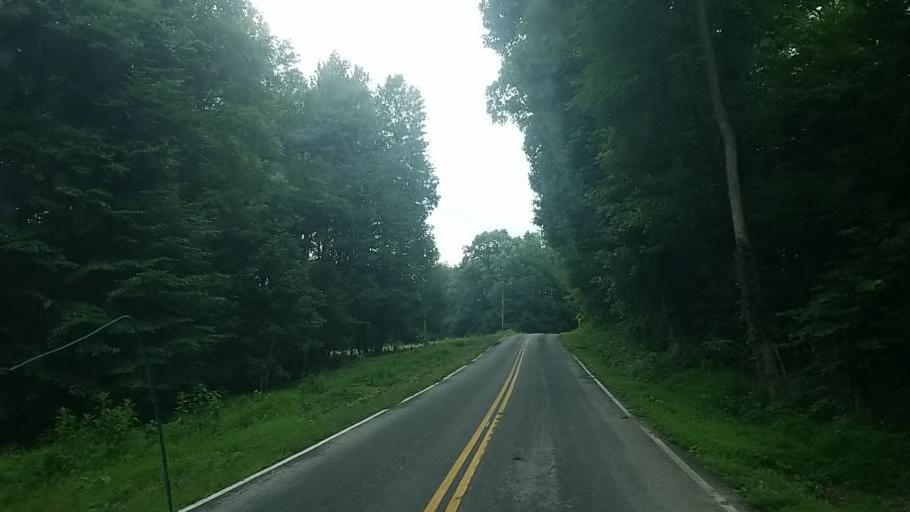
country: US
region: Ohio
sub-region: Muskingum County
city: Frazeysburg
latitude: 40.1658
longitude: -82.2574
